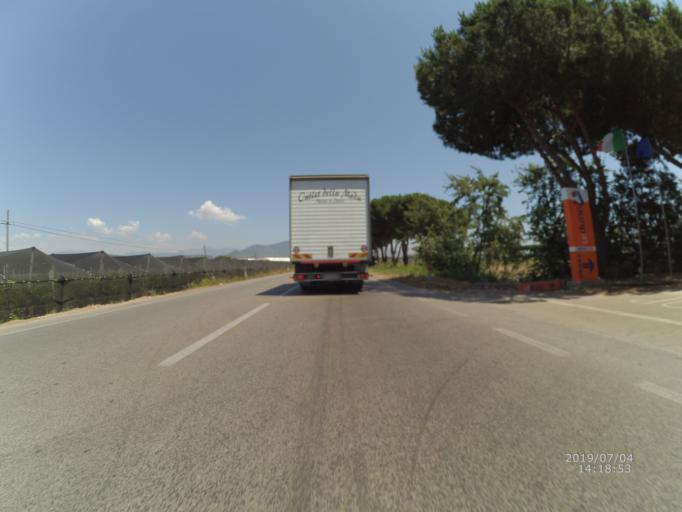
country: IT
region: Latium
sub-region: Provincia di Latina
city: Sperlonga
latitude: 41.2868
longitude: 13.3812
